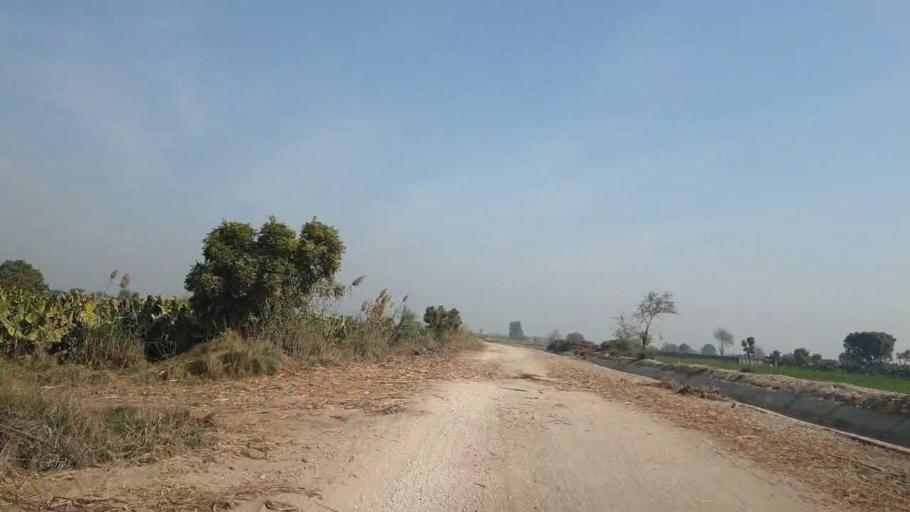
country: PK
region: Sindh
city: Tando Allahyar
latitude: 25.5965
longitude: 68.7209
